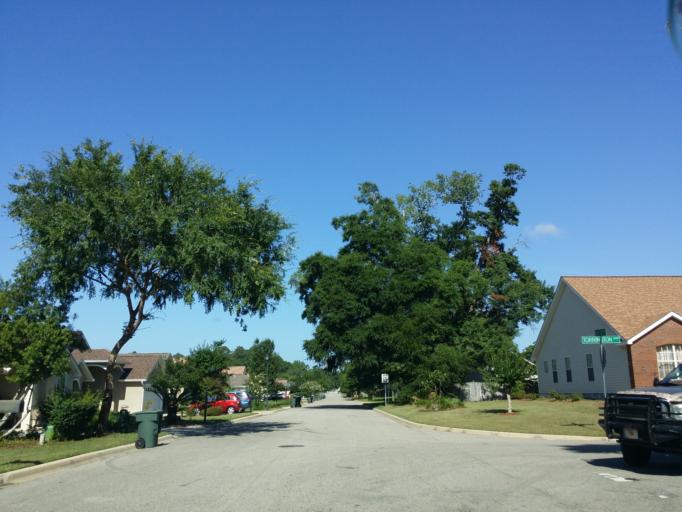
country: US
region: Florida
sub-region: Leon County
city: Tallahassee
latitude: 30.4563
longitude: -84.2154
